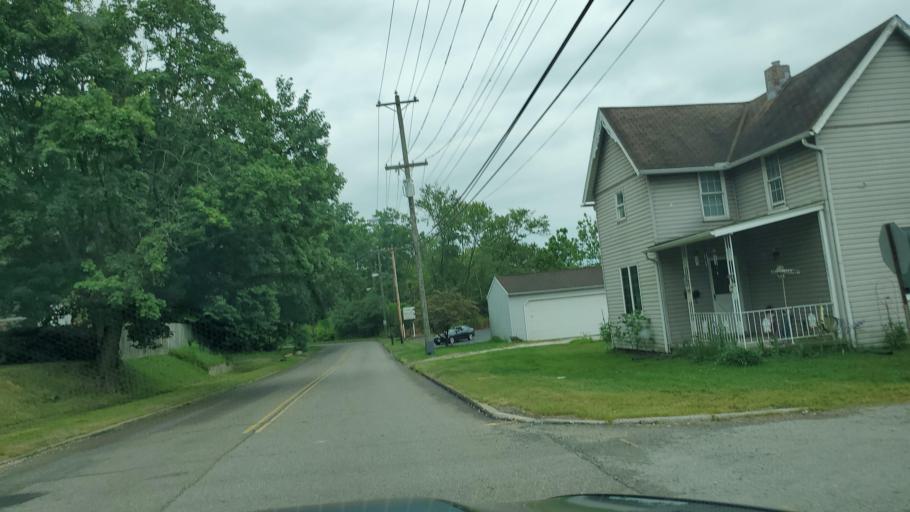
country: US
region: Ohio
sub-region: Trumbull County
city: Niles
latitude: 41.1721
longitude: -80.7486
